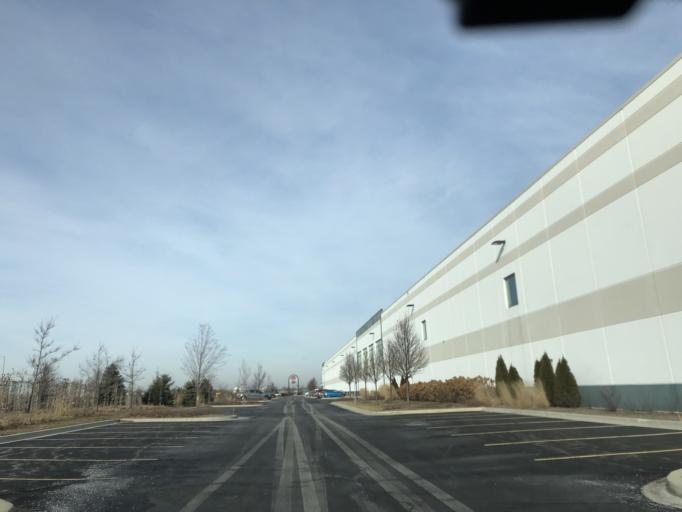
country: US
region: Illinois
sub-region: DuPage County
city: Woodridge
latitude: 41.7150
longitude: -88.0315
